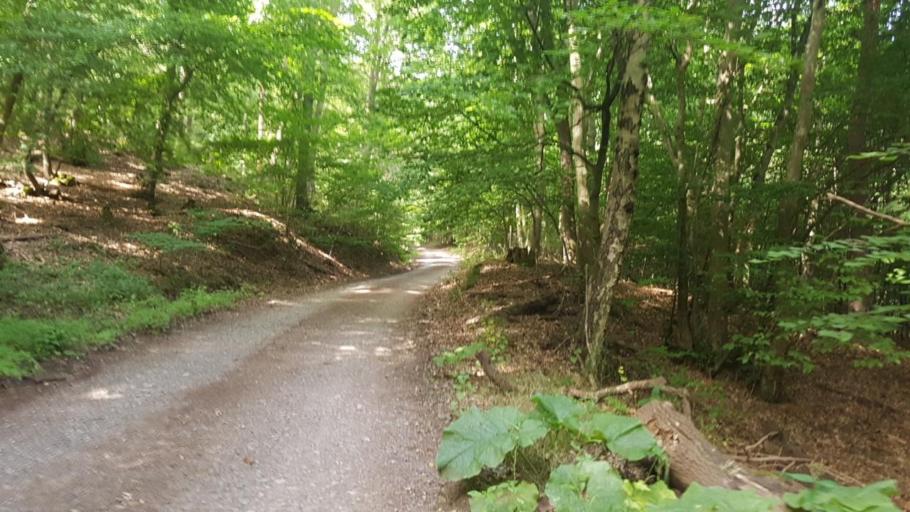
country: DE
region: North Rhine-Westphalia
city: Heimbach
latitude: 50.6235
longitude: 6.5007
